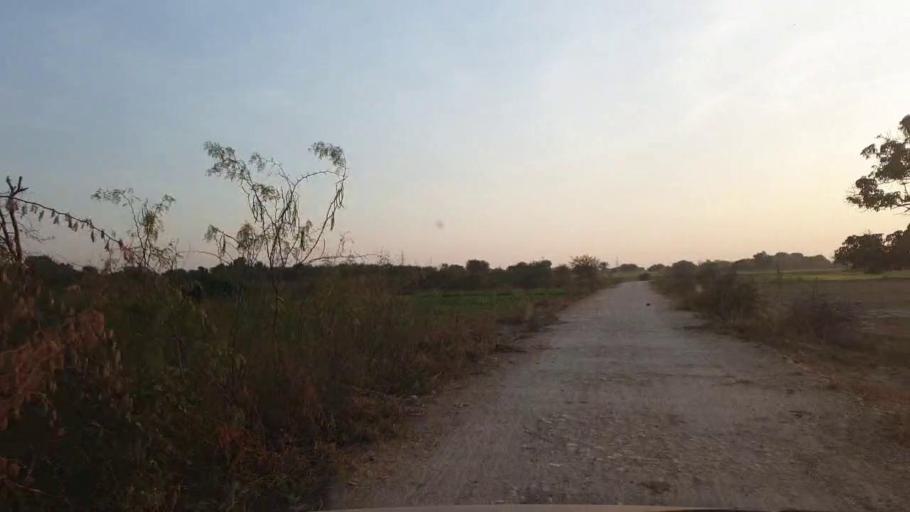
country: PK
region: Sindh
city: Chambar
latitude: 25.2836
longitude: 68.8184
